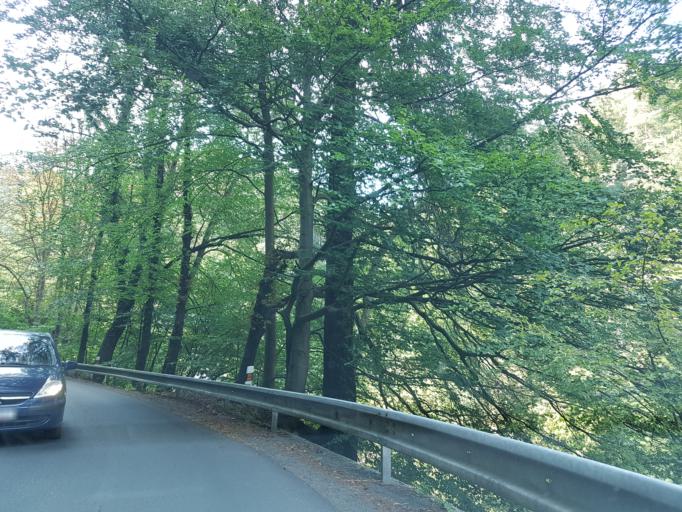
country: CZ
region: Ustecky
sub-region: Okres Decin
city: Decin
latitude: 50.8742
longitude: 14.2486
